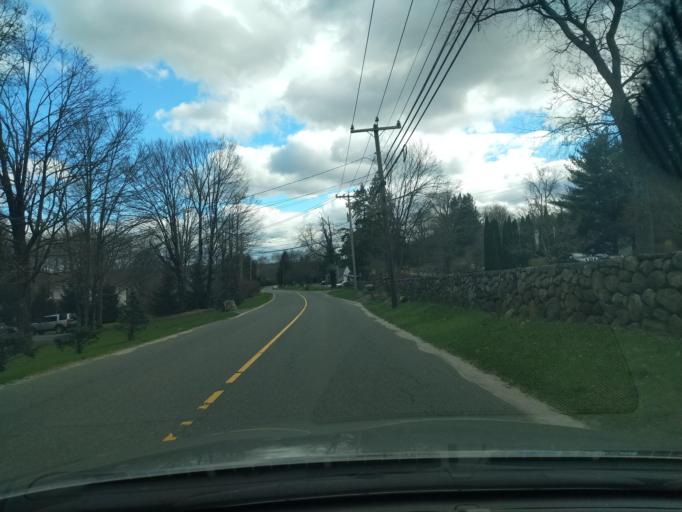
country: US
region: Connecticut
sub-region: Fairfield County
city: Bethel
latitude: 41.3912
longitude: -73.3732
